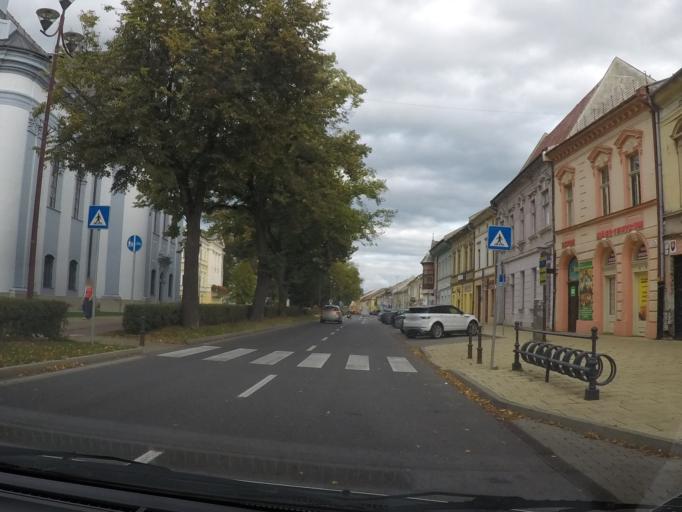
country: SK
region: Kosicky
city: Spisska Nova Ves
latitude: 48.9443
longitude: 20.5655
